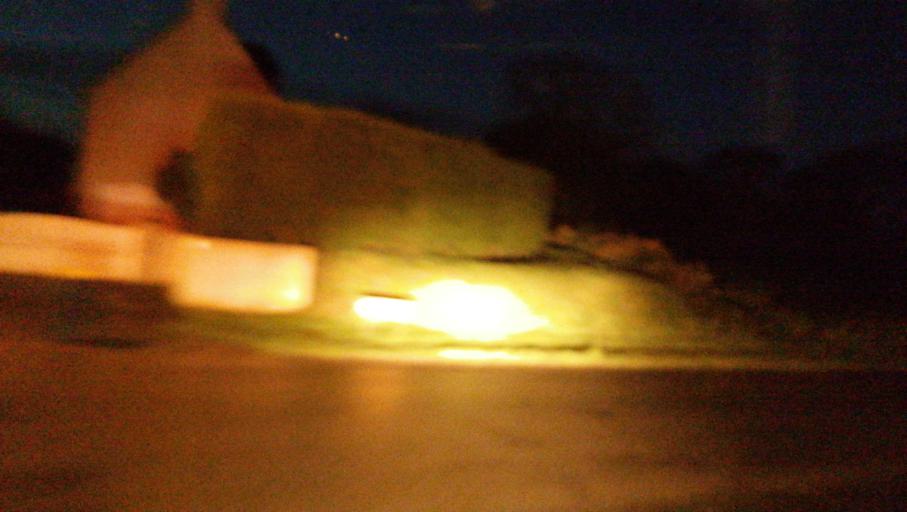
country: FR
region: Brittany
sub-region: Departement des Cotes-d'Armor
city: Plouha
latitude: 48.6742
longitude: -2.9434
